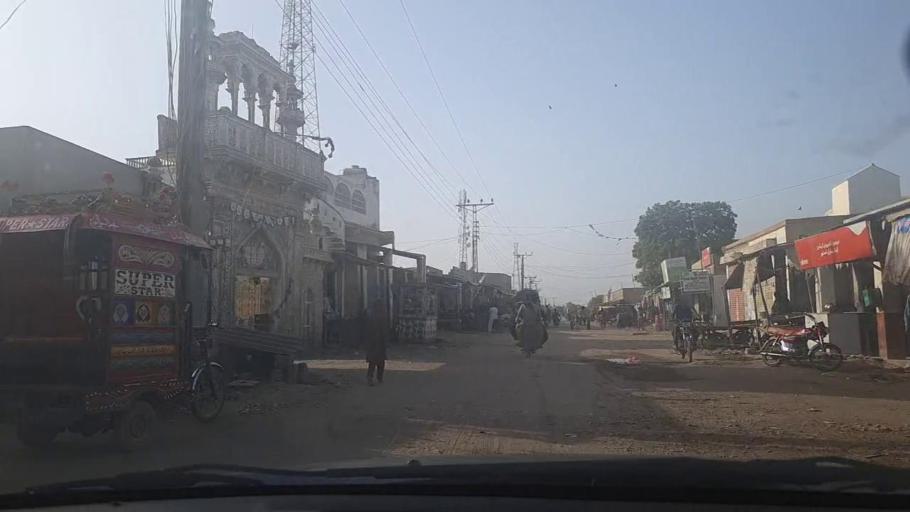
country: PK
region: Sindh
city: Keti Bandar
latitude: 24.3019
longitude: 67.6059
